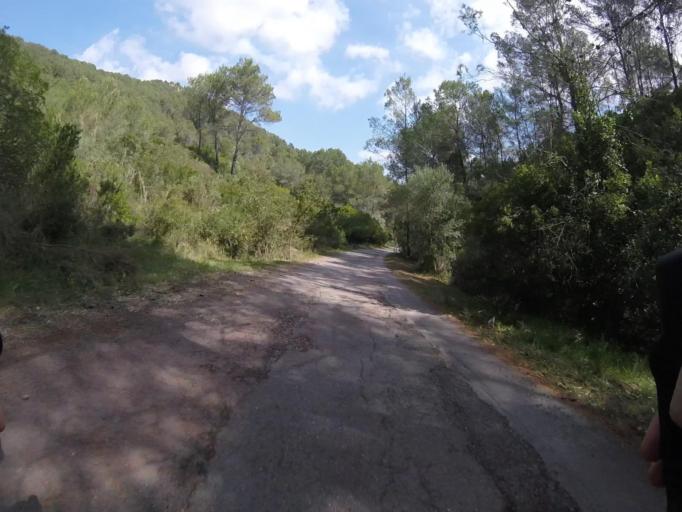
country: ES
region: Valencia
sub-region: Provincia de Castello
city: Cabanes
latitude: 40.1059
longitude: 0.0393
